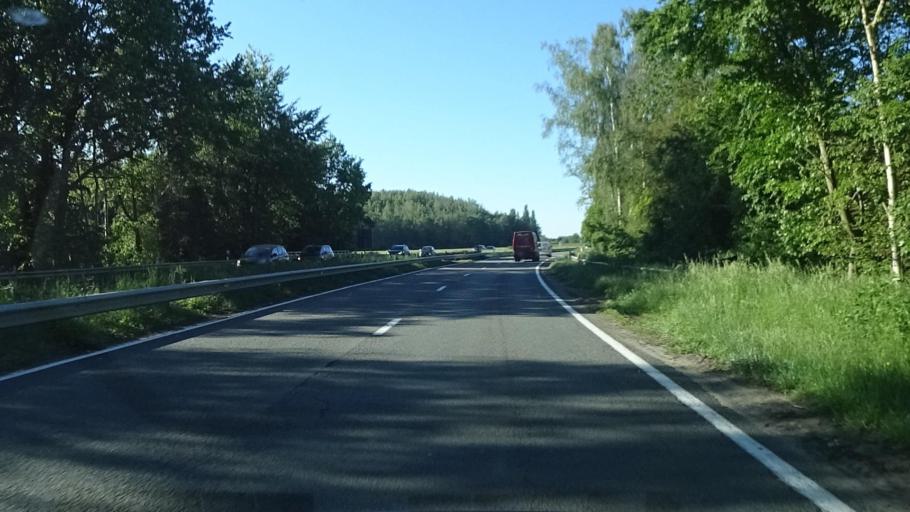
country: BE
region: Wallonia
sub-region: Province du Hainaut
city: Roeulx
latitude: 50.4732
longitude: 4.1382
